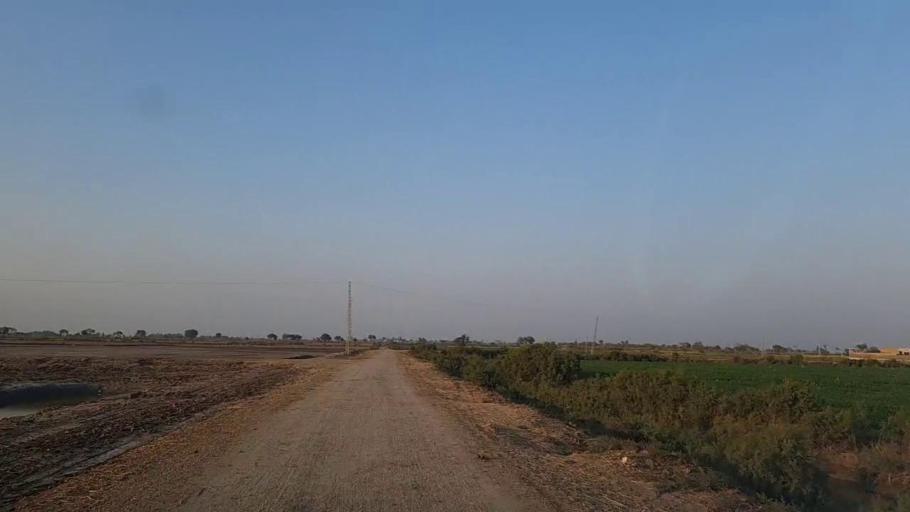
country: PK
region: Sindh
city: Bandhi
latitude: 26.5473
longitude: 68.3167
